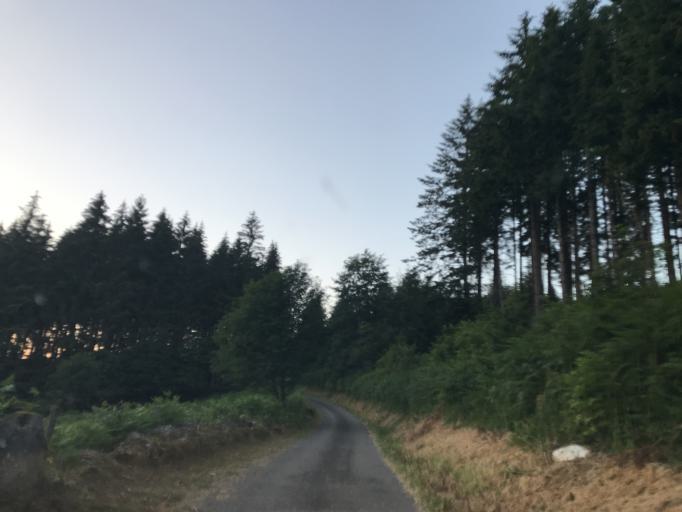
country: FR
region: Rhone-Alpes
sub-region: Departement de la Loire
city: Noiretable
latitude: 45.7800
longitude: 3.6924
